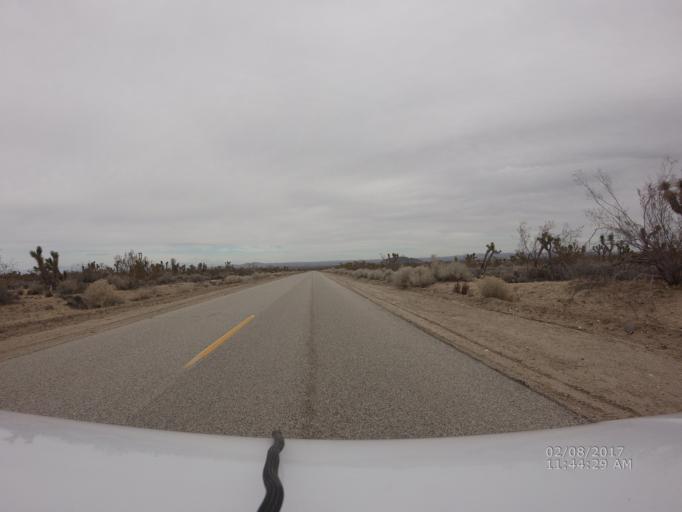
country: US
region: California
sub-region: San Bernardino County
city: Pinon Hills
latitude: 34.4869
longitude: -117.7481
